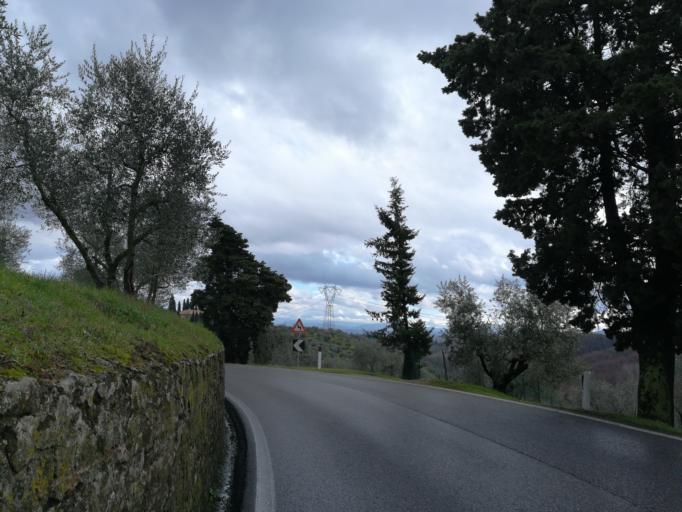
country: IT
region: Tuscany
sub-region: Provincia di Prato
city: Poggio A Caiano
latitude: 43.8036
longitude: 11.0370
